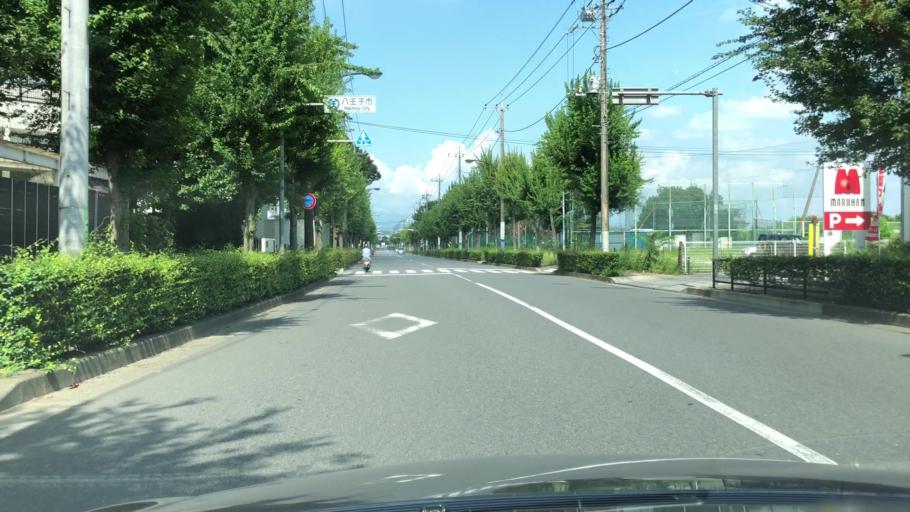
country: JP
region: Tokyo
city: Hino
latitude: 35.6870
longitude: 139.3778
